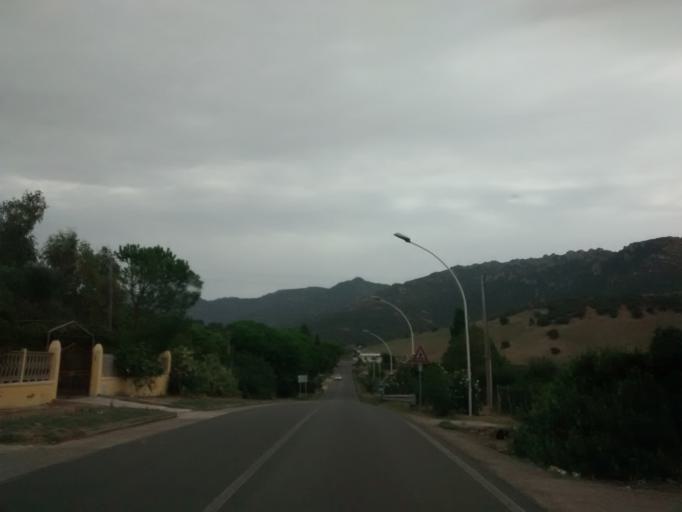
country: IT
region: Sardinia
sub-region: Provincia di Cagliari
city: Villasimius
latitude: 39.1409
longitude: 9.4292
